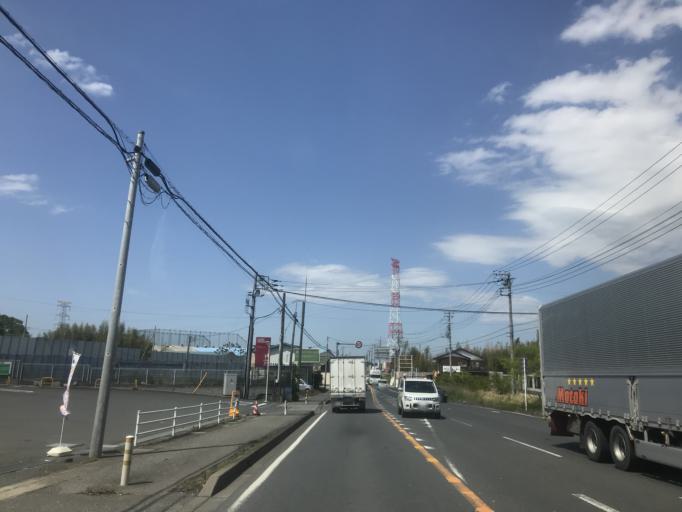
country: JP
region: Chiba
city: Noda
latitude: 35.9705
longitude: 139.8839
